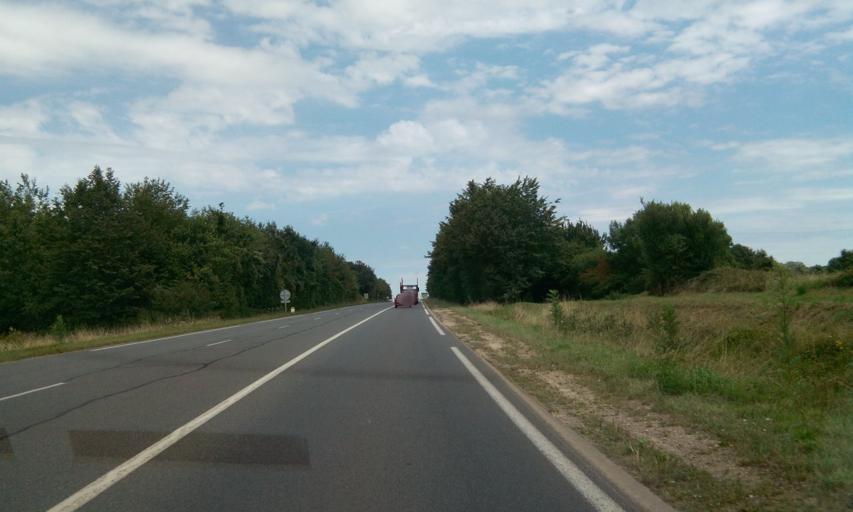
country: FR
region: Poitou-Charentes
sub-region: Departement des Deux-Sevres
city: Melle
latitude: 46.2166
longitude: -0.1573
